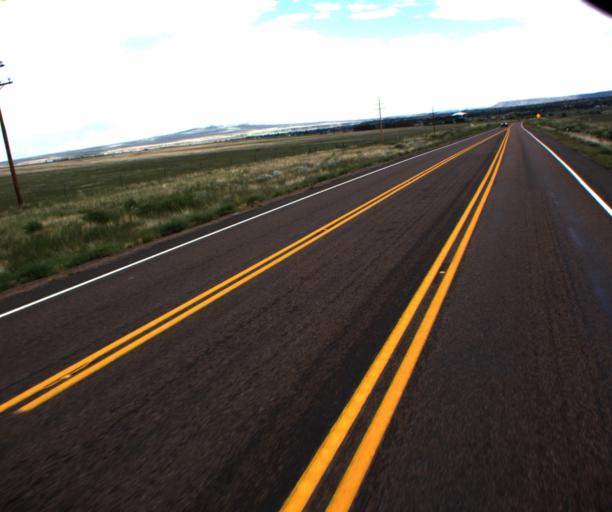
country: US
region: Arizona
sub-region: Apache County
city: Eagar
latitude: 34.1100
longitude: -109.3249
